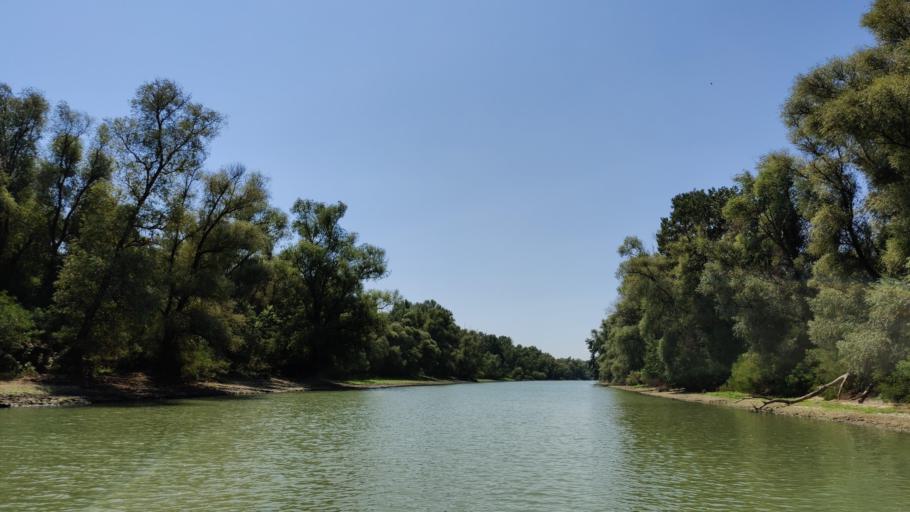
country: RO
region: Tulcea
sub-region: Comuna Nufaru
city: Nufaru
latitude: 45.2257
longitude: 28.8868
